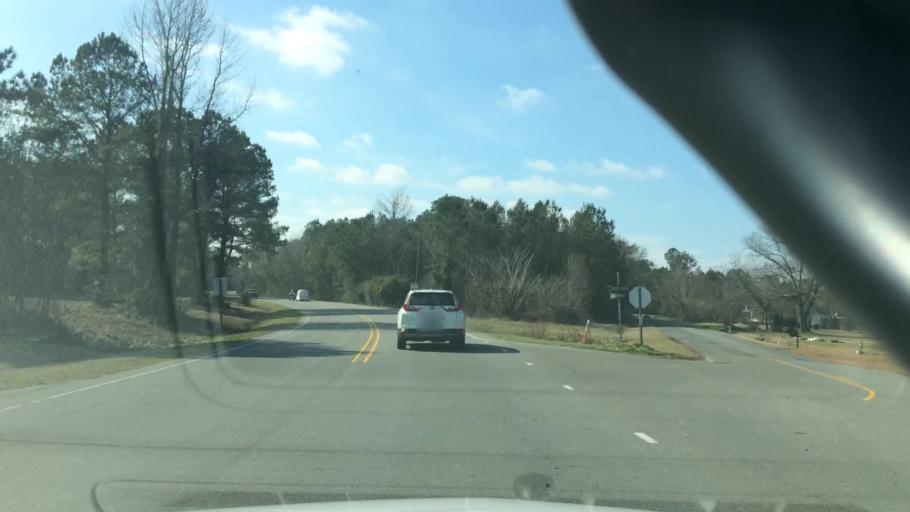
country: US
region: North Carolina
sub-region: Duplin County
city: Beulaville
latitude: 34.8336
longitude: -77.8263
